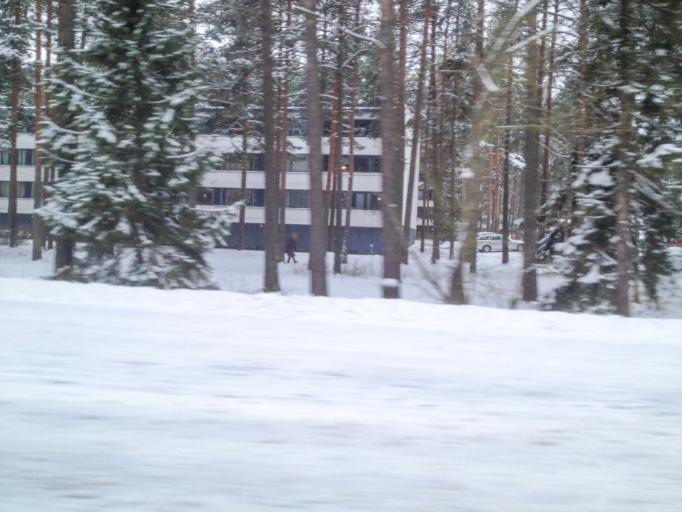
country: FI
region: Uusimaa
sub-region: Helsinki
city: Vantaa
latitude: 60.2203
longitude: 25.1340
